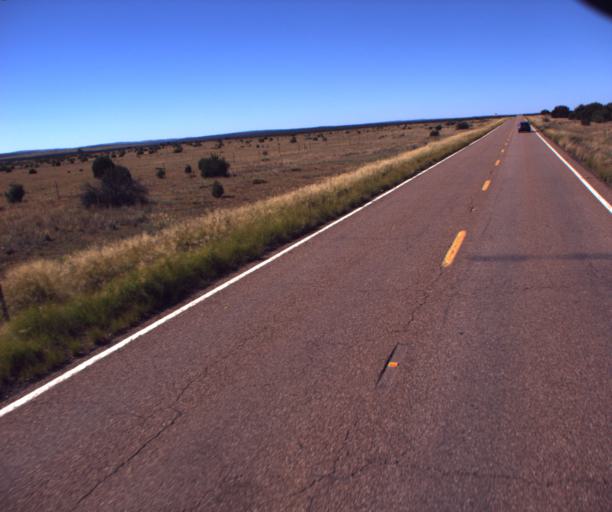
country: US
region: Arizona
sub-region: Navajo County
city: Heber-Overgaard
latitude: 34.4754
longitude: -110.3511
